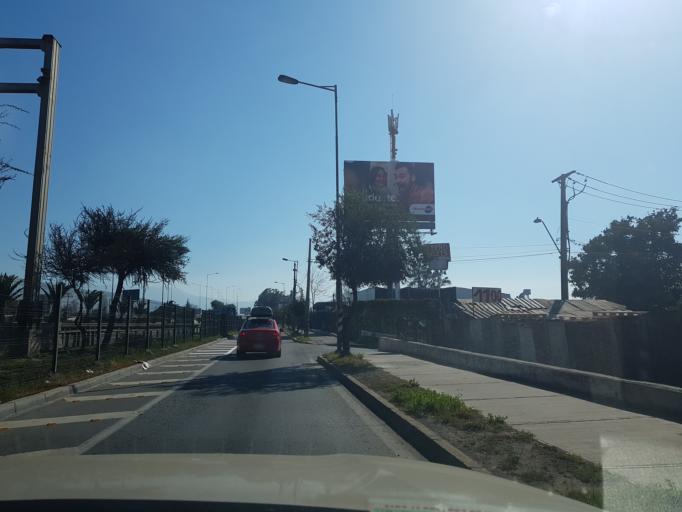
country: CL
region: Santiago Metropolitan
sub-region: Provincia de Santiago
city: Lo Prado
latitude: -33.3719
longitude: -70.7335
